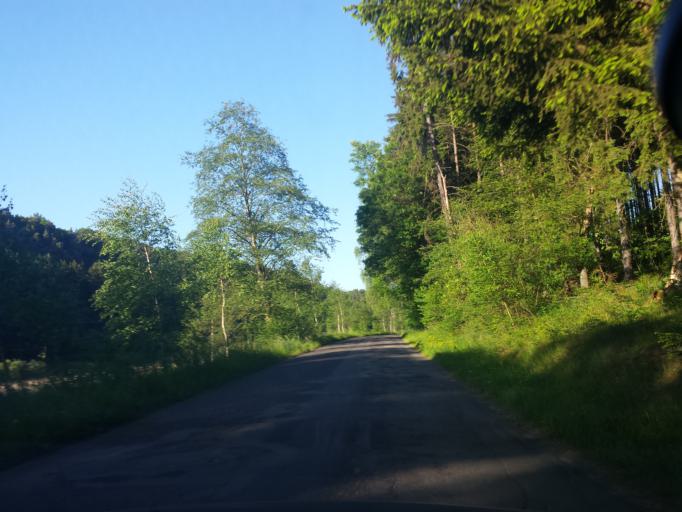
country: CZ
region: Central Bohemia
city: Mseno
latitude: 50.4627
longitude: 14.6066
